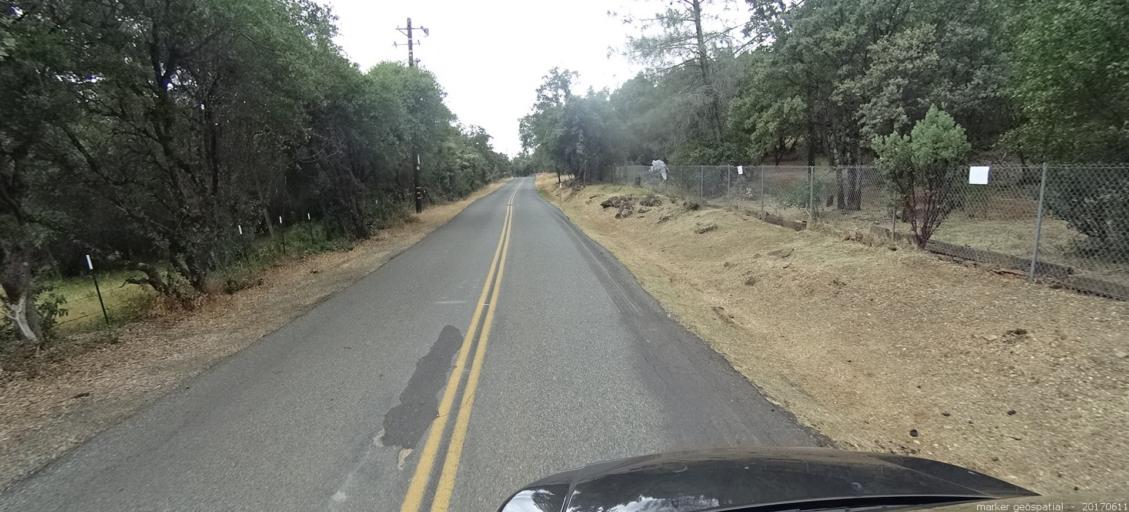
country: US
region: California
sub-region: Butte County
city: Berry Creek
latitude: 39.6375
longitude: -121.5281
